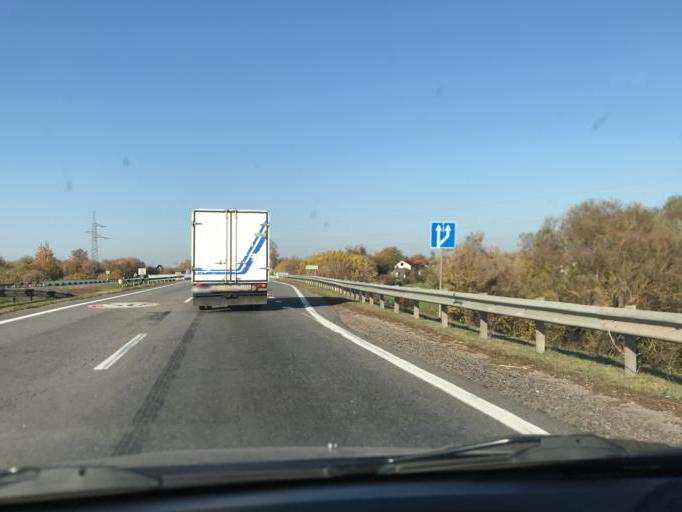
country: BY
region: Minsk
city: Dukora
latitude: 53.6663
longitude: 27.9383
